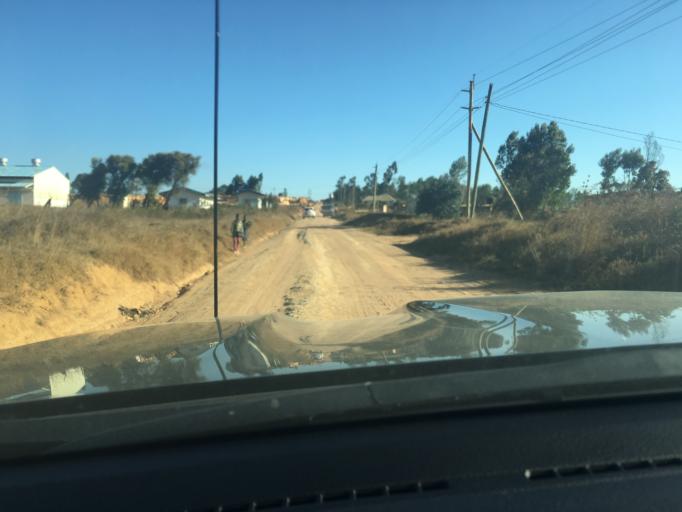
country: TZ
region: Iringa
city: Makungu
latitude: -8.4133
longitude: 35.4204
